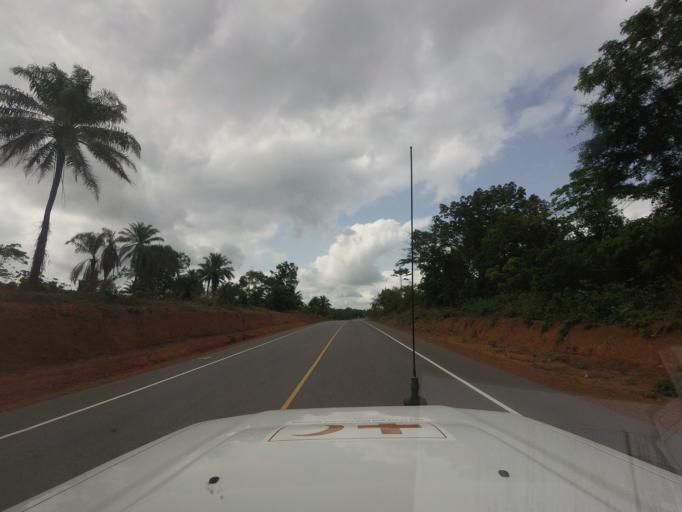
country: LR
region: Nimba
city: Sanniquellie
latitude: 7.1757
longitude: -9.0333
